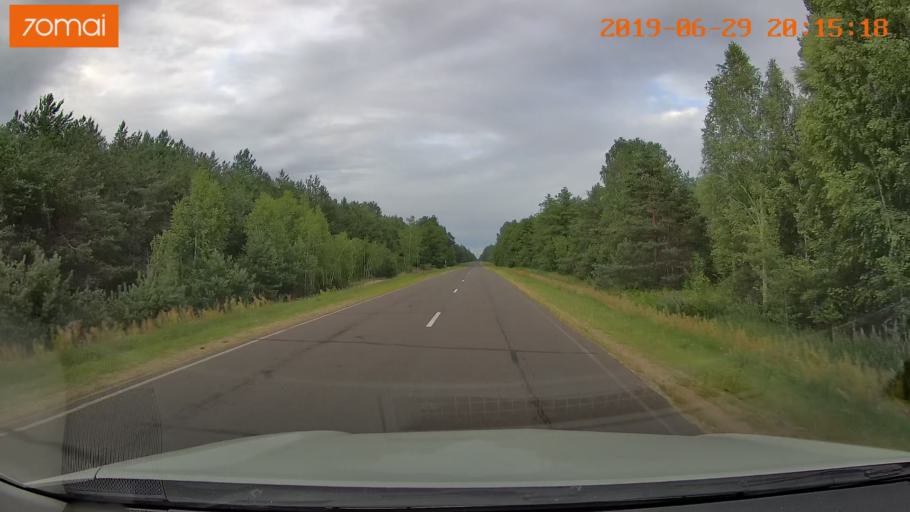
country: BY
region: Brest
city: Asnyezhytsy
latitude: 52.3733
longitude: 26.1730
